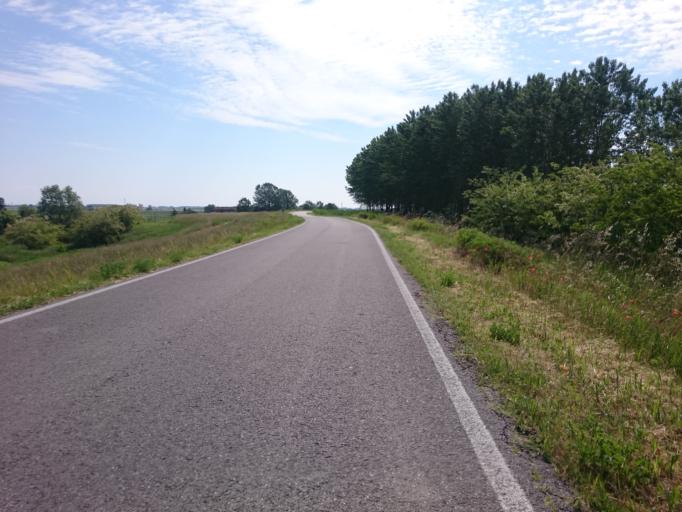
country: IT
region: Veneto
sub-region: Provincia di Rovigo
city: Ariano
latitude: 44.9621
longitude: 12.1098
